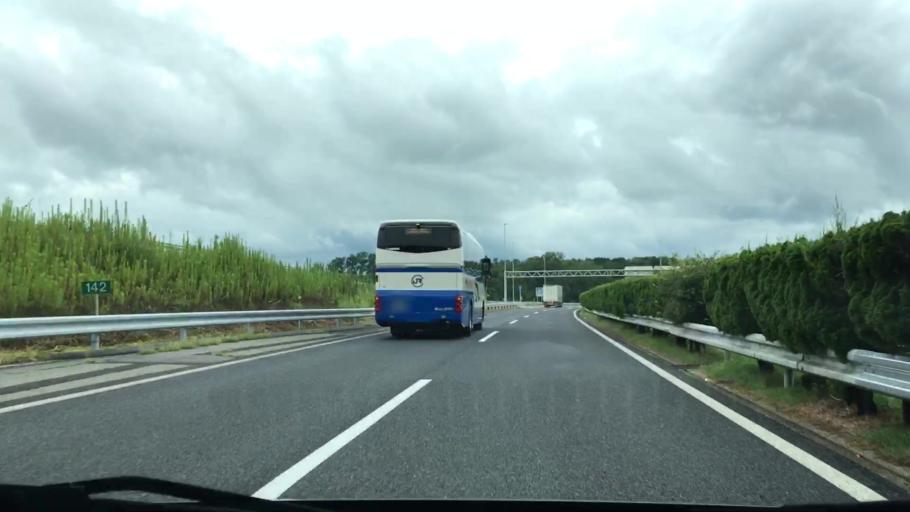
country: JP
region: Okayama
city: Tsuyama
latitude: 35.0352
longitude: 134.1383
